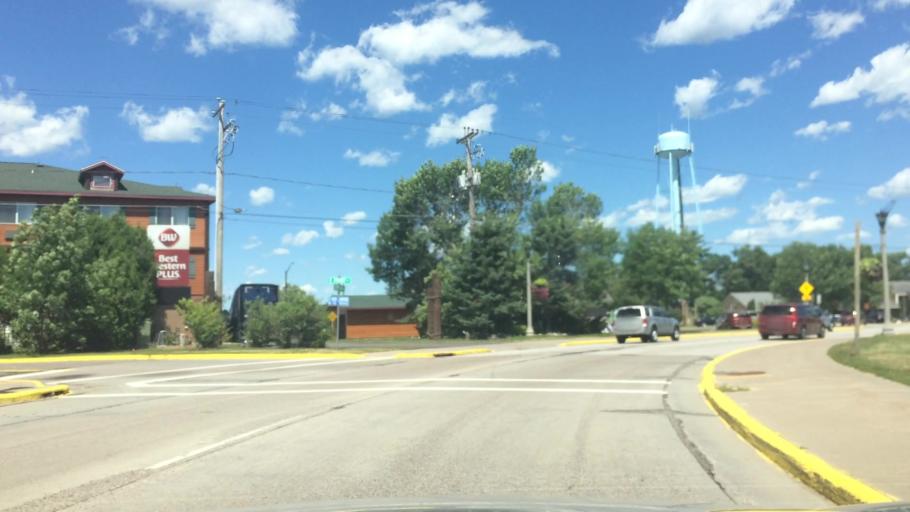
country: US
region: Wisconsin
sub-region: Vilas County
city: Lac du Flambeau
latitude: 45.8713
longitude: -89.7085
